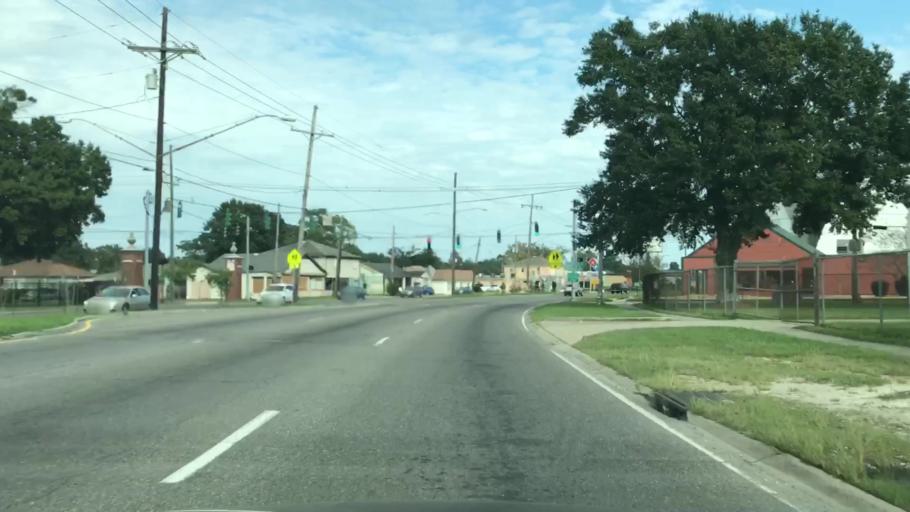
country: US
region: Louisiana
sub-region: Jefferson Parish
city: Jefferson
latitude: 29.9627
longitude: -90.1665
